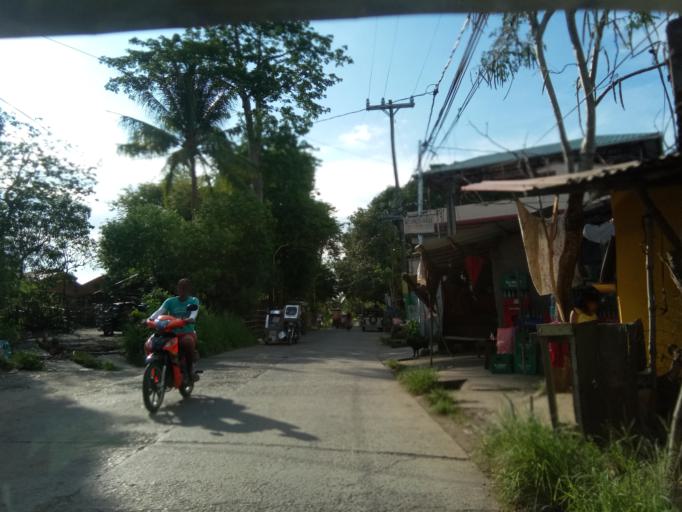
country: PH
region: Calabarzon
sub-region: Province of Cavite
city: Biga
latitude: 14.2831
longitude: 120.9455
